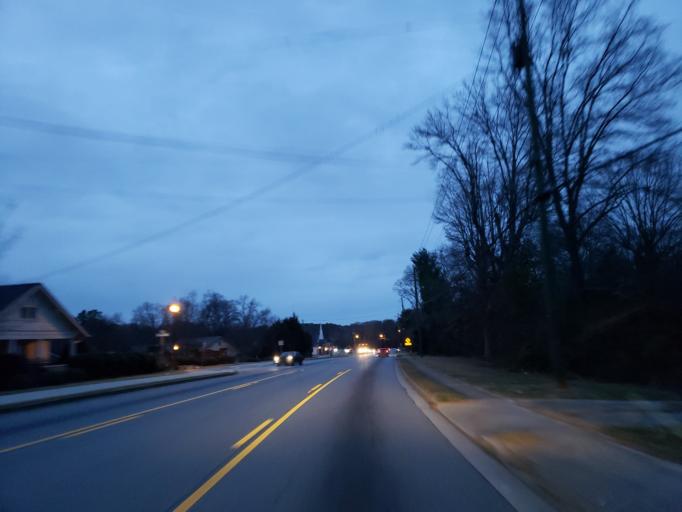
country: US
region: Georgia
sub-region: Cobb County
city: Mableton
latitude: 33.8428
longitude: -84.5813
